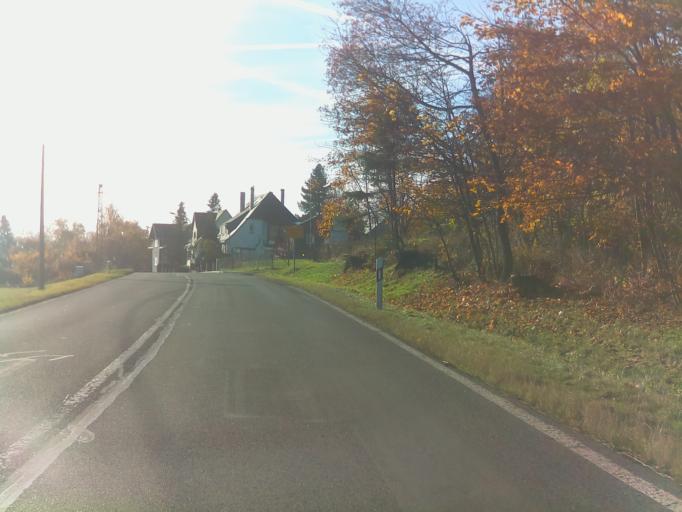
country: DE
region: Thuringia
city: Reichmannsdorf
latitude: 50.5556
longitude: 11.2587
